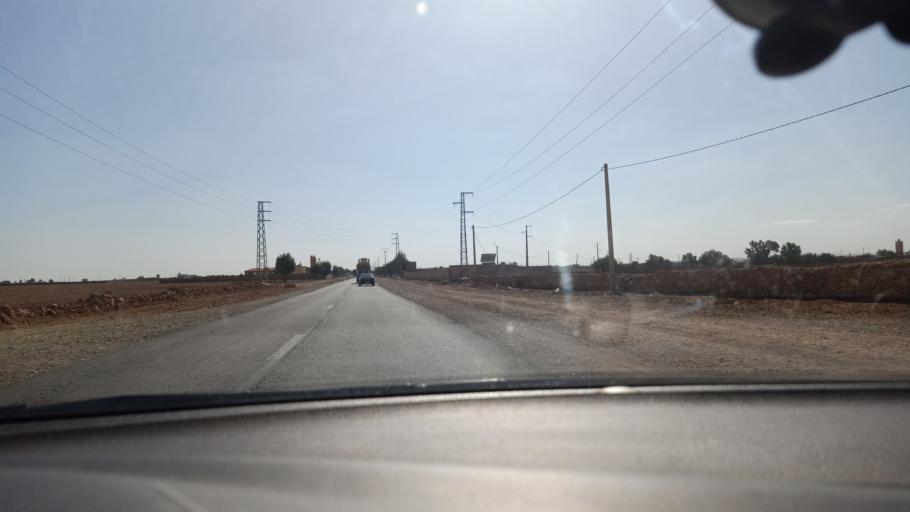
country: MA
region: Doukkala-Abda
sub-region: Safi
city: Youssoufia
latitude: 32.1065
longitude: -8.6102
